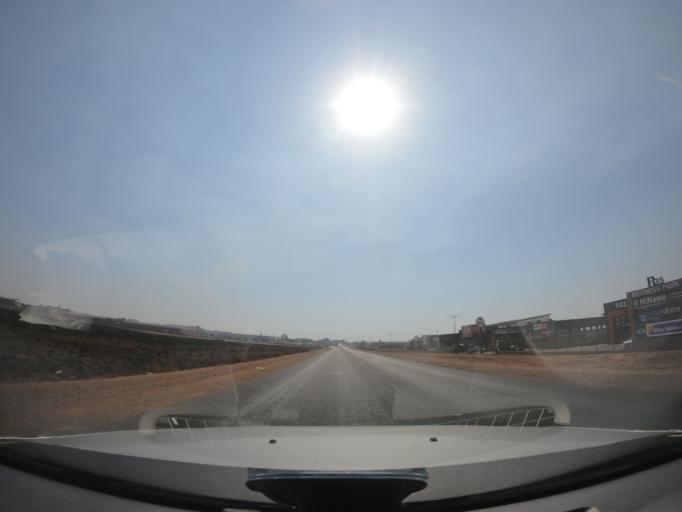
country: ZA
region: Mpumalanga
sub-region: Nkangala District Municipality
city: Middelburg
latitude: -25.8118
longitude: 29.4616
